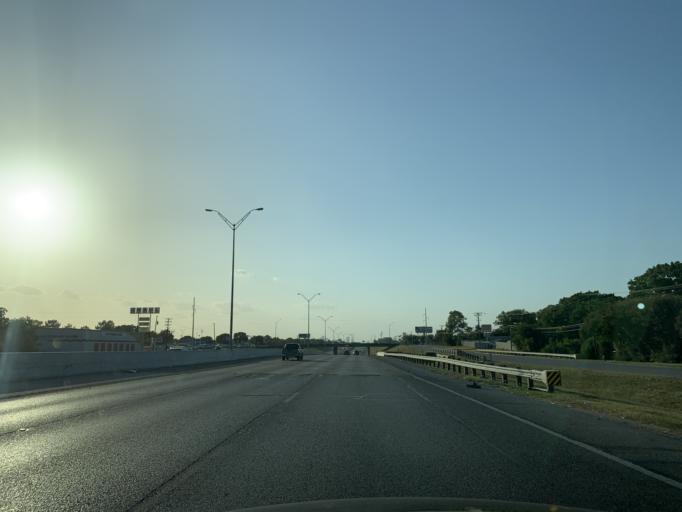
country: US
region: Texas
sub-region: Dallas County
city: Balch Springs
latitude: 32.7227
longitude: -96.6974
